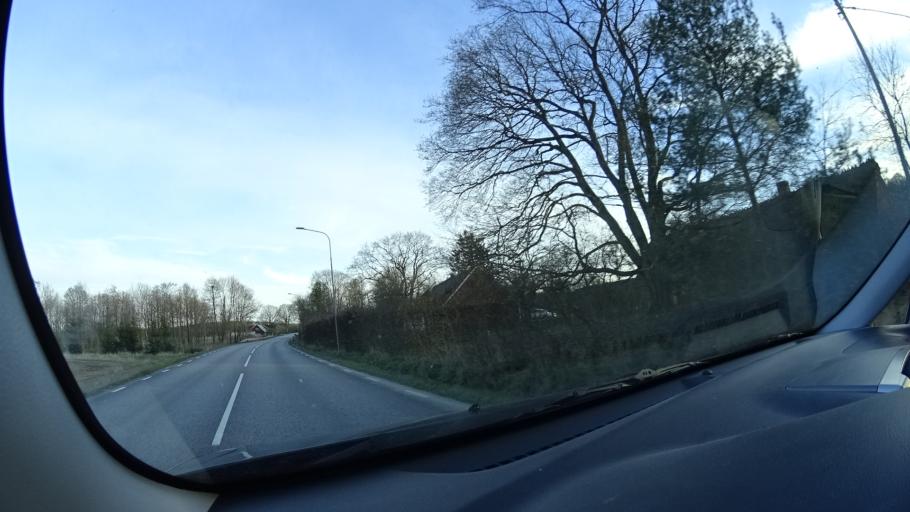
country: SE
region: Skane
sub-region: Eslovs Kommun
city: Stehag
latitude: 55.9748
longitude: 13.3283
